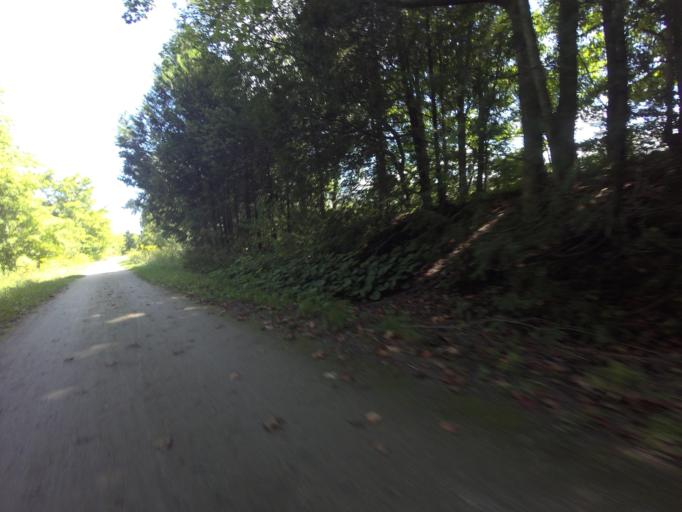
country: CA
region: Ontario
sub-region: Wellington County
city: Guelph
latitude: 43.7853
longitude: -80.3223
